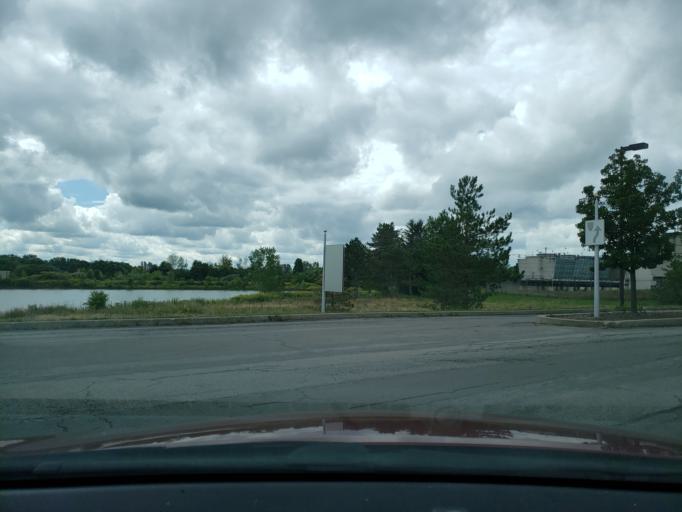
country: US
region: New York
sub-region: Monroe County
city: North Gates
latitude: 43.1477
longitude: -77.7345
